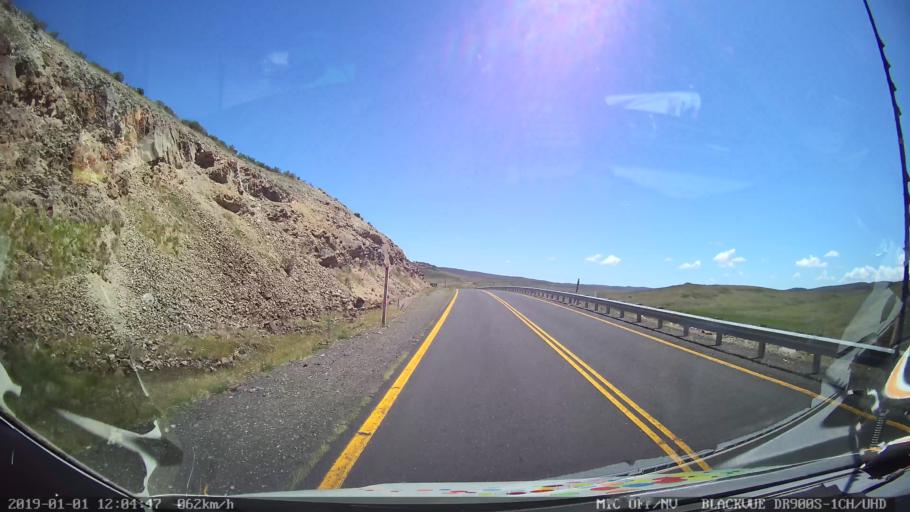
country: AU
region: New South Wales
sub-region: Snowy River
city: Jindabyne
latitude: -35.8640
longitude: 148.4960
